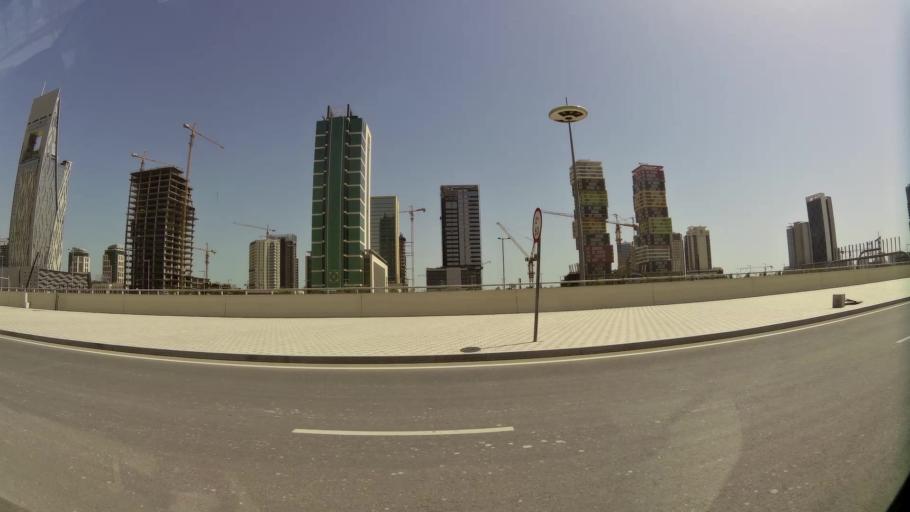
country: QA
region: Baladiyat ad Dawhah
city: Doha
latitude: 25.3877
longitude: 51.5185
